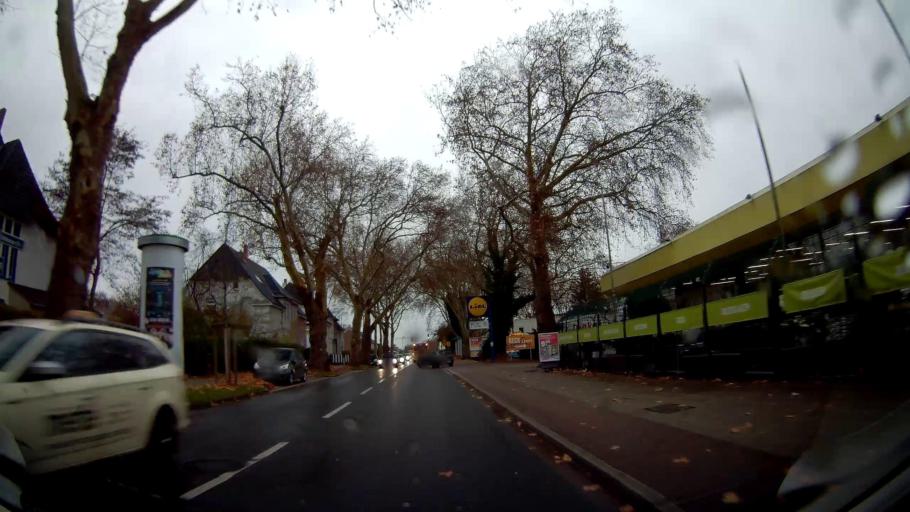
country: DE
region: North Rhine-Westphalia
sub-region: Regierungsbezirk Munster
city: Gelsenkirchen
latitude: 51.4737
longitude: 7.0816
